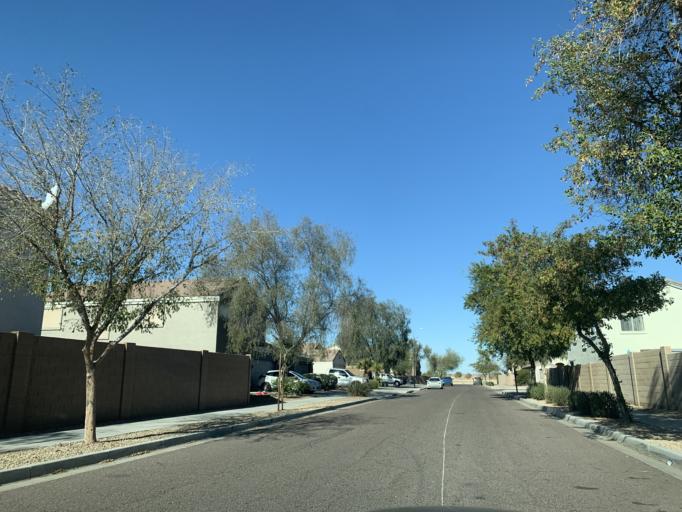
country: US
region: Arizona
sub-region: Maricopa County
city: Laveen
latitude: 33.3945
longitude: -112.1278
